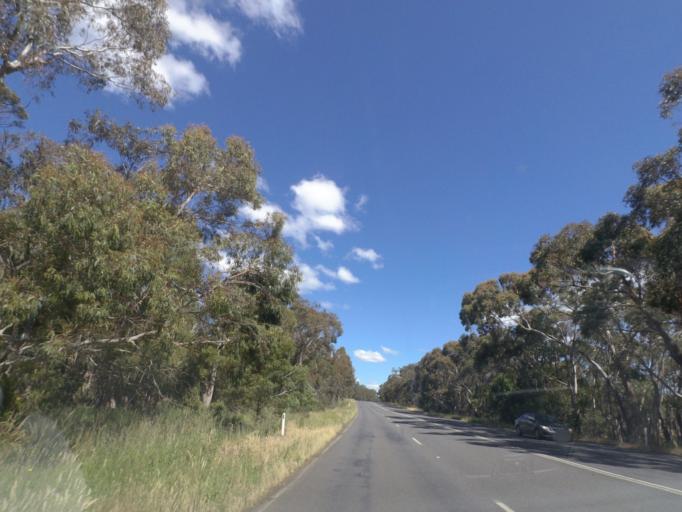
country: AU
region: Victoria
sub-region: Hume
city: Sunbury
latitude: -37.4431
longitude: 144.5680
